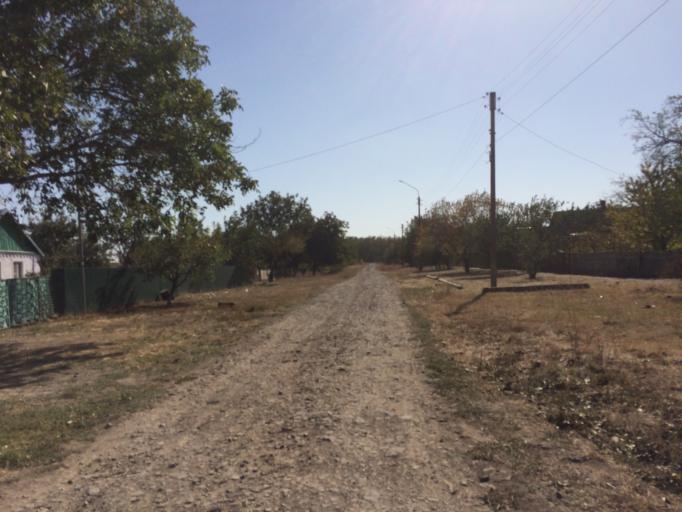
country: RU
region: Rostov
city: Gigant
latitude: 46.5226
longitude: 41.1882
